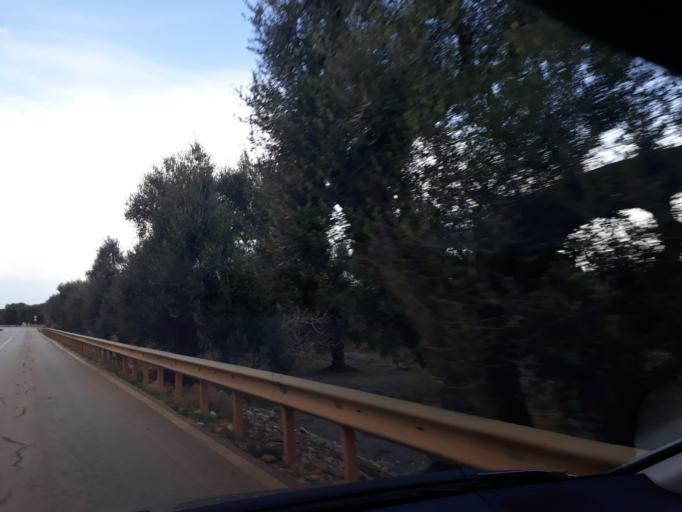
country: IT
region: Apulia
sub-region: Provincia di Brindisi
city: Pezze di Greco
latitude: 40.8113
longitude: 17.3847
